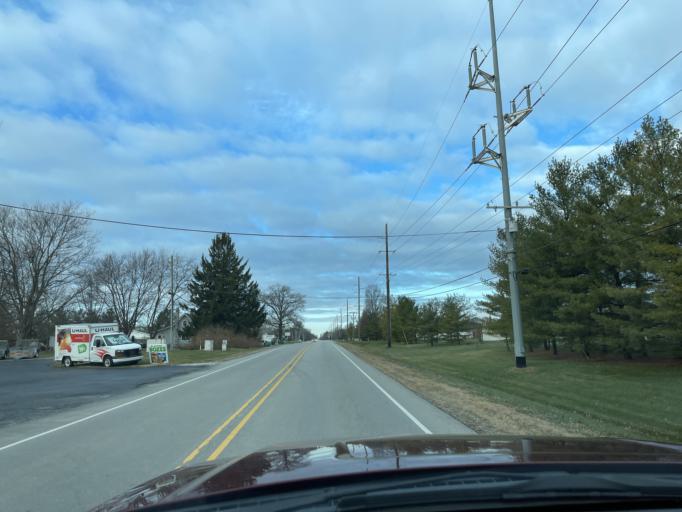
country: US
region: Indiana
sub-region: Hendricks County
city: Avon
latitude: 39.7623
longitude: -86.4341
